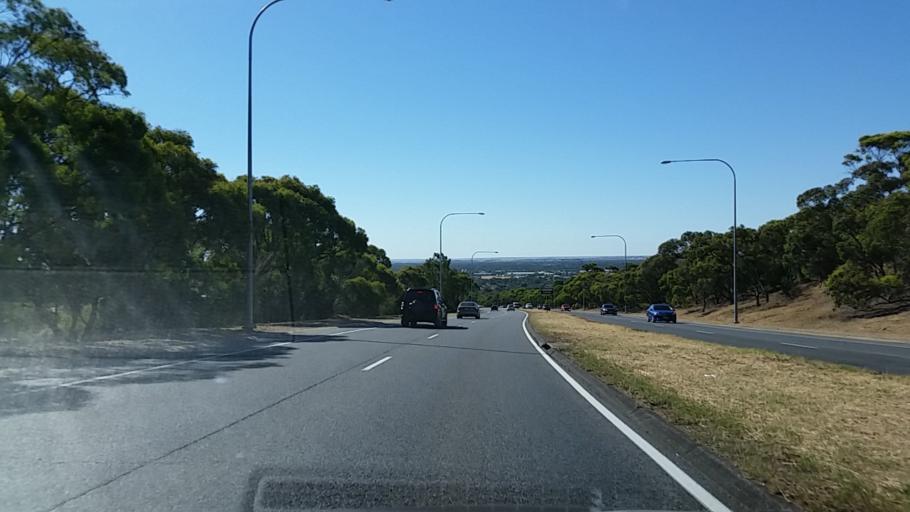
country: AU
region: South Australia
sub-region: Tea Tree Gully
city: Modbury
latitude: -34.8071
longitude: 138.6682
